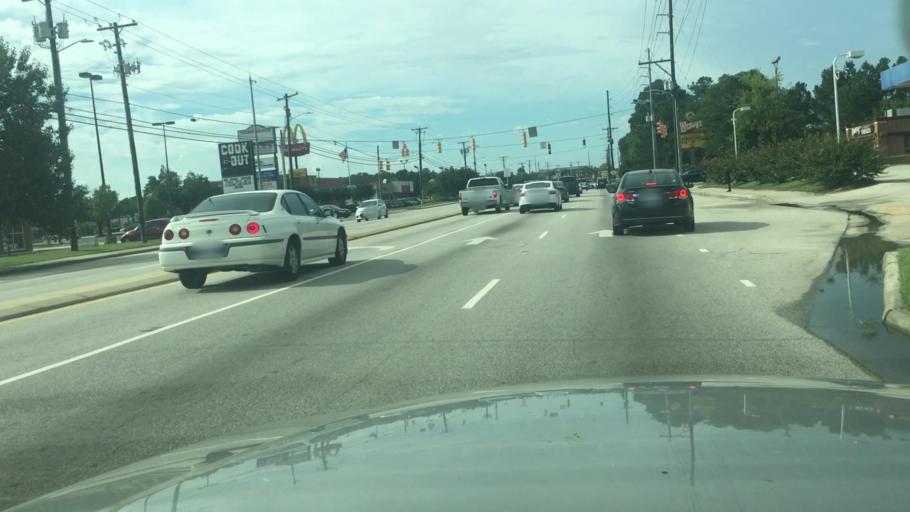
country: US
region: North Carolina
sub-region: Cumberland County
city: Fayetteville
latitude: 35.1116
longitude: -78.8793
